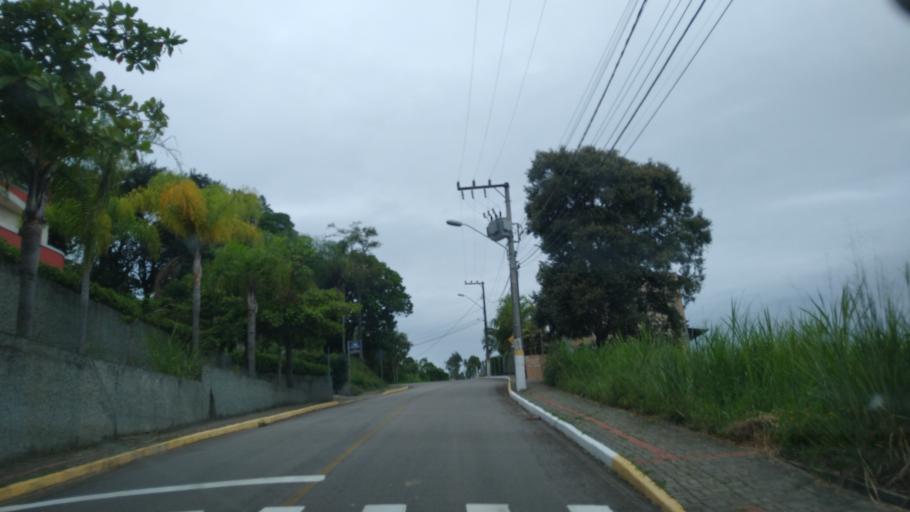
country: BR
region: Santa Catarina
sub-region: Itapema
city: Itapema
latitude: -27.0903
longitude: -48.6035
